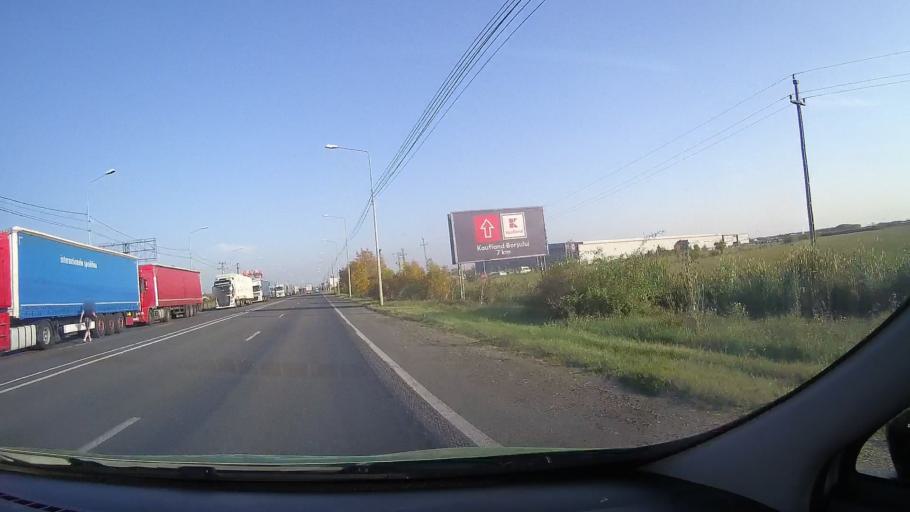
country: RO
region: Bihor
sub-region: Comuna Bors
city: Bors
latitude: 47.1082
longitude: 21.8222
